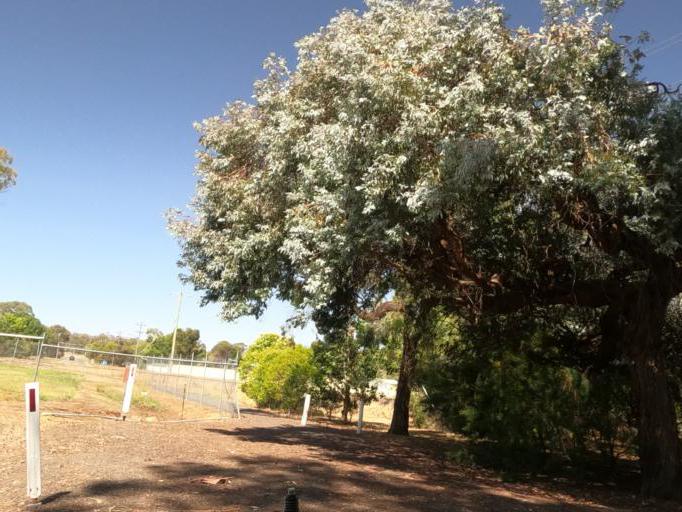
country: AU
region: New South Wales
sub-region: Corowa Shire
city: Mulwala
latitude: -35.9882
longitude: 146.0006
